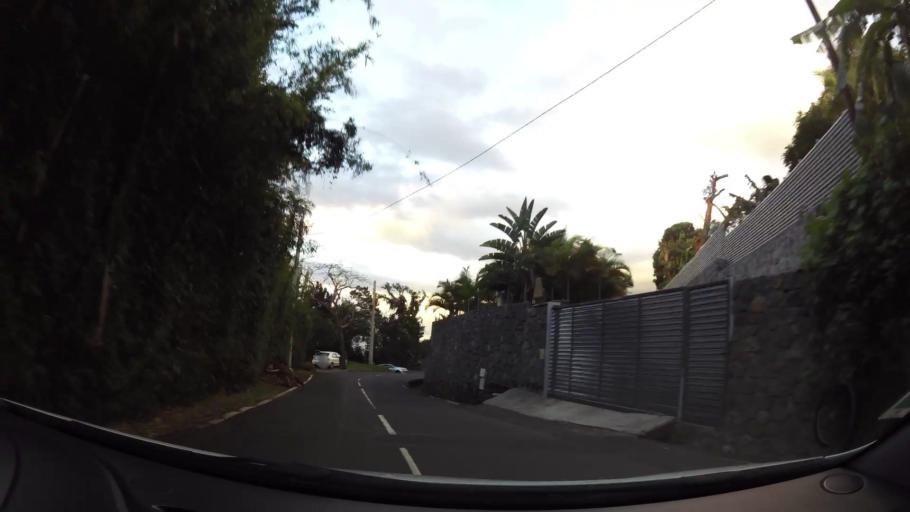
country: RE
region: Reunion
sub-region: Reunion
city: Saint-Denis
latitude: -20.9110
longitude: 55.4620
